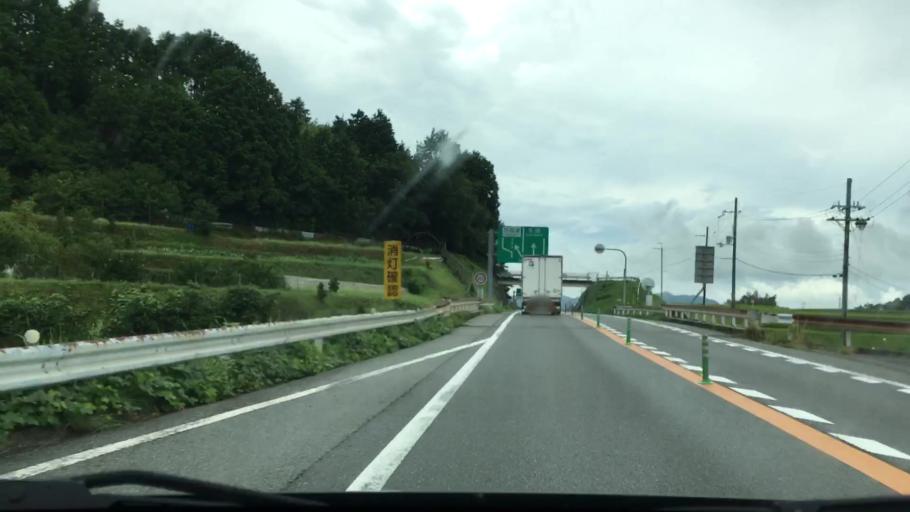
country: JP
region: Hyogo
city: Himeji
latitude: 34.9622
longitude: 134.7697
